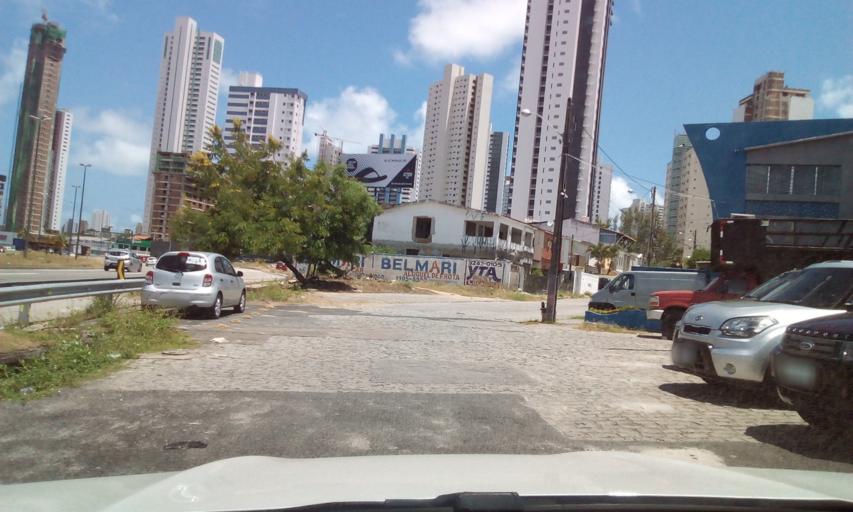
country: BR
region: Paraiba
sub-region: Joao Pessoa
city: Joao Pessoa
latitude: -7.1181
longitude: -34.8433
